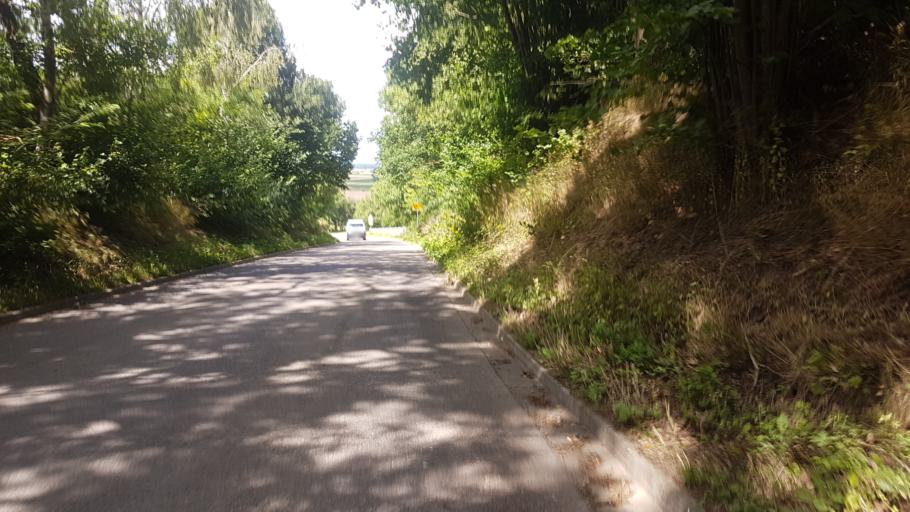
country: DE
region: Bavaria
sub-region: Regierungsbezirk Mittelfranken
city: Geslau
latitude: 49.3458
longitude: 10.3312
